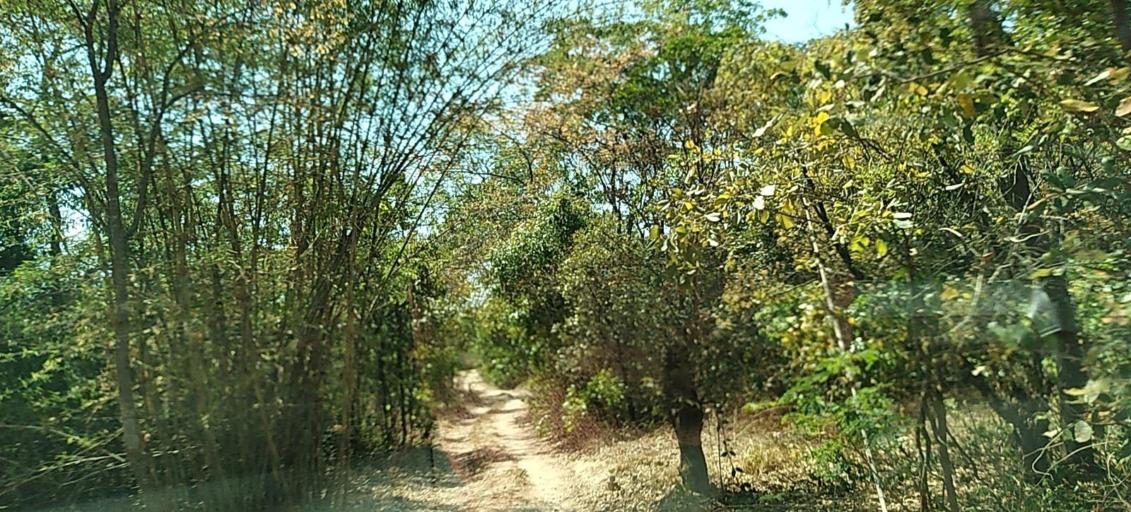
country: ZM
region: Copperbelt
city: Chililabombwe
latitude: -12.2859
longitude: 27.8831
